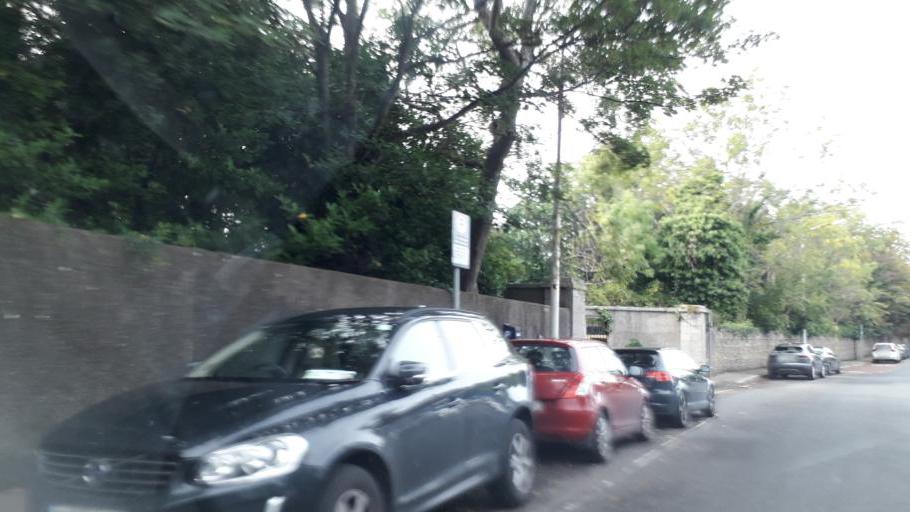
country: IE
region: Leinster
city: Cabinteely
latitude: 53.2619
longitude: -6.1530
